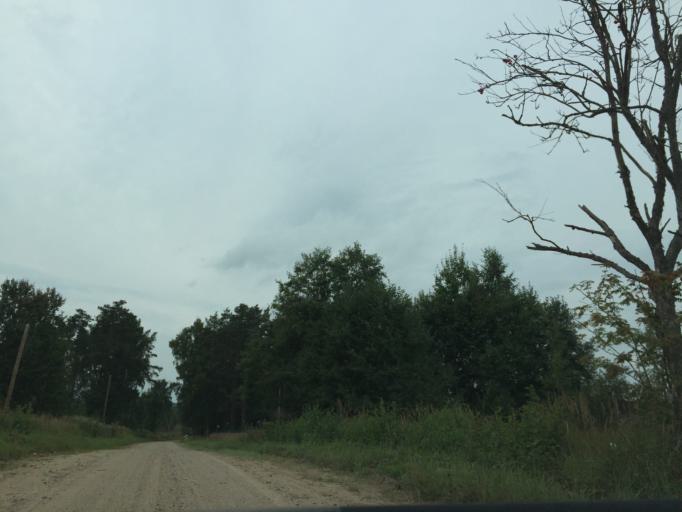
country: LV
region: Zilupes
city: Zilupe
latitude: 56.3529
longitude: 28.1841
